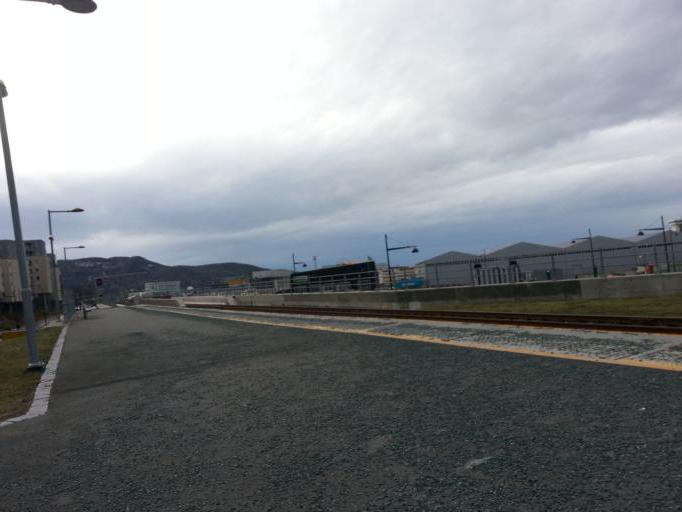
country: NO
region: Sor-Trondelag
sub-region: Trondheim
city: Trondheim
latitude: 63.4372
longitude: 10.4165
